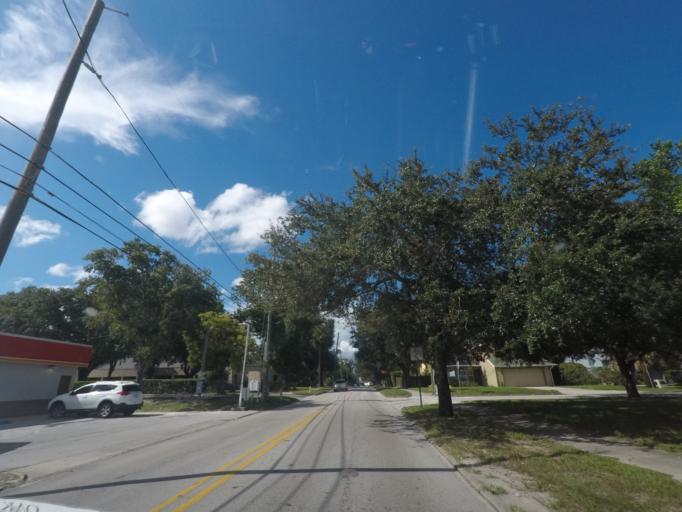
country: US
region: Florida
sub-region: Orange County
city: Fairview Shores
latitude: 28.5825
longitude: -81.3731
